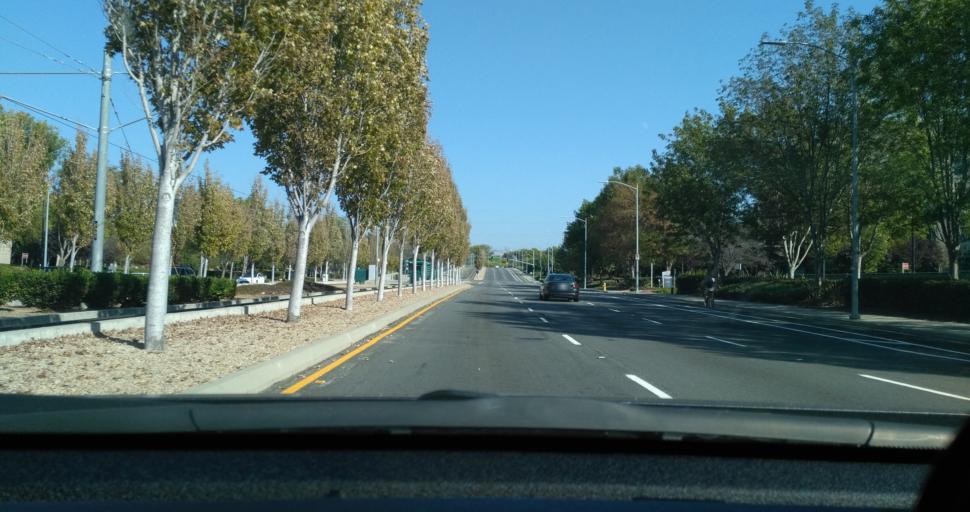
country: US
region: California
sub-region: Santa Clara County
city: Milpitas
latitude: 37.4130
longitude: -121.9304
